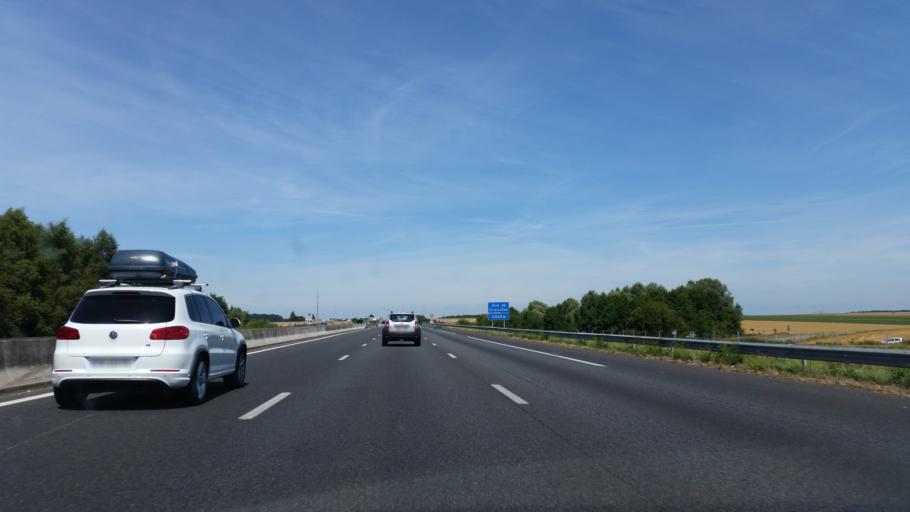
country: FR
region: Nord-Pas-de-Calais
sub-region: Departement du Pas-de-Calais
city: Croisilles
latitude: 50.1646
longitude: 2.8740
